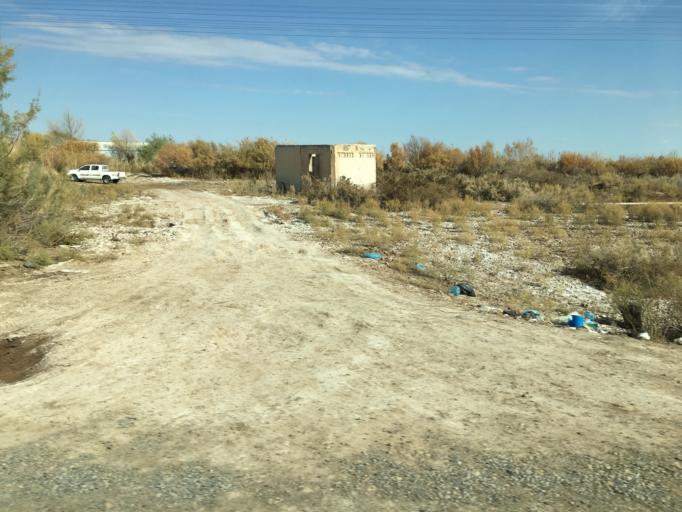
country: TM
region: Ahal
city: Tejen
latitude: 37.2586
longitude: 61.1751
